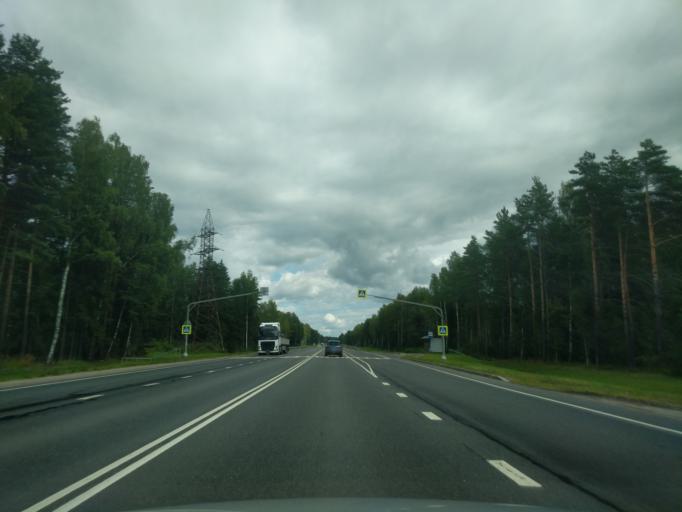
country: RU
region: Jaroslavl
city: Nekrasovskoye
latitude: 57.5873
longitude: 40.2945
